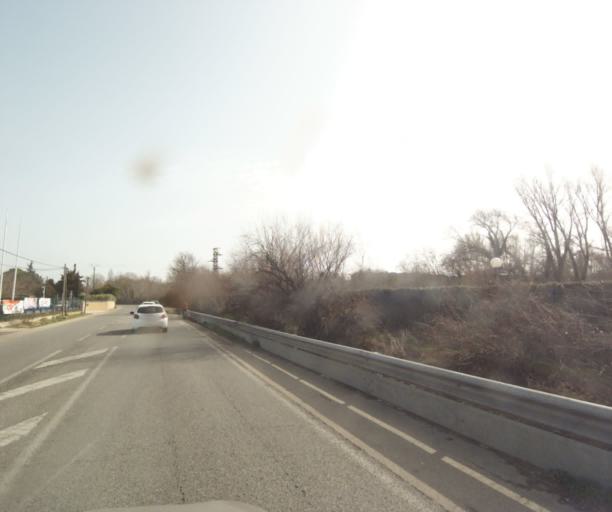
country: FR
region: Provence-Alpes-Cote d'Azur
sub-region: Departement des Bouches-du-Rhone
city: Aix-en-Provence
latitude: 43.5105
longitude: 5.4150
